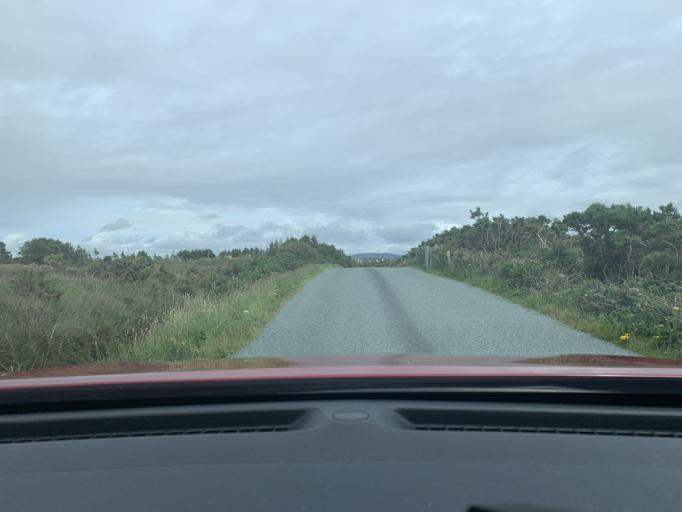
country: IE
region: Ulster
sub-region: County Donegal
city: Dungloe
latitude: 54.9594
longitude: -8.3704
